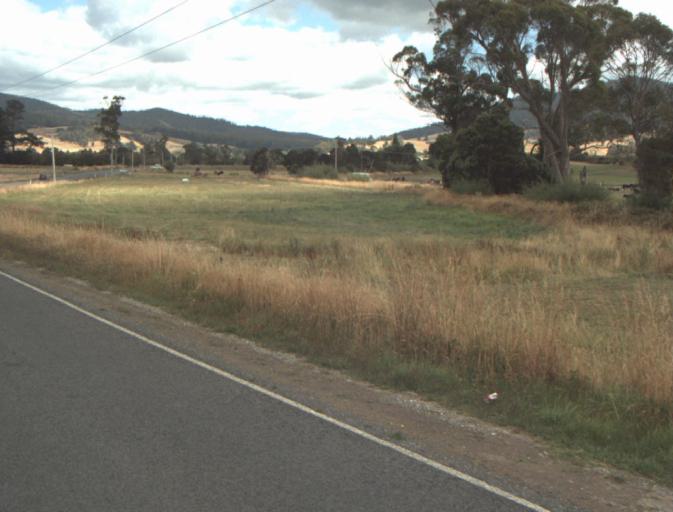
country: AU
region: Tasmania
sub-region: Launceston
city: Mayfield
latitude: -41.2362
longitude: 147.2147
